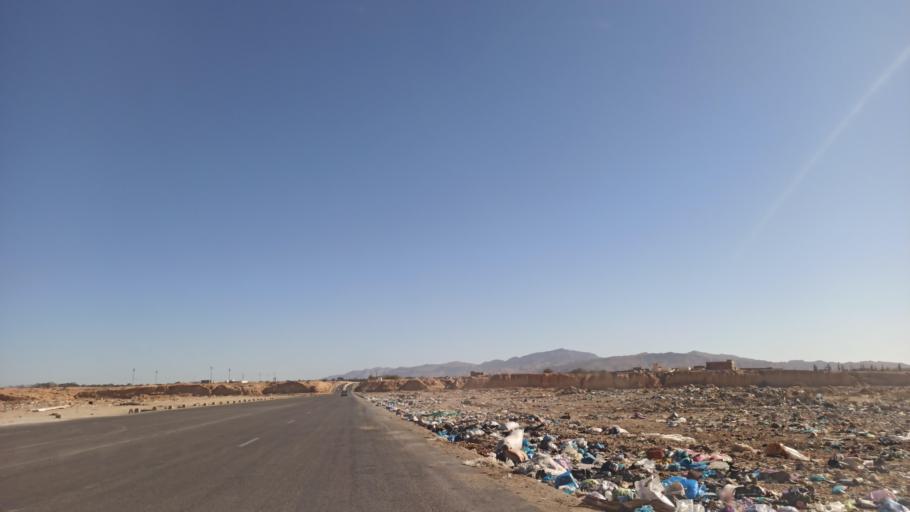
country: TN
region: Gafsa
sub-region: Gafsa Municipality
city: Gafsa
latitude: 34.4340
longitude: 8.8023
